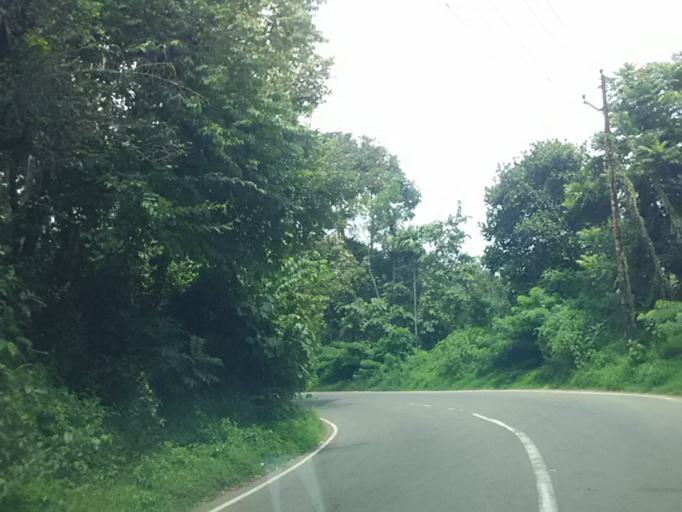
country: IN
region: Kerala
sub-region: Wayanad
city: Kalpetta
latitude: 11.5835
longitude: 76.0629
